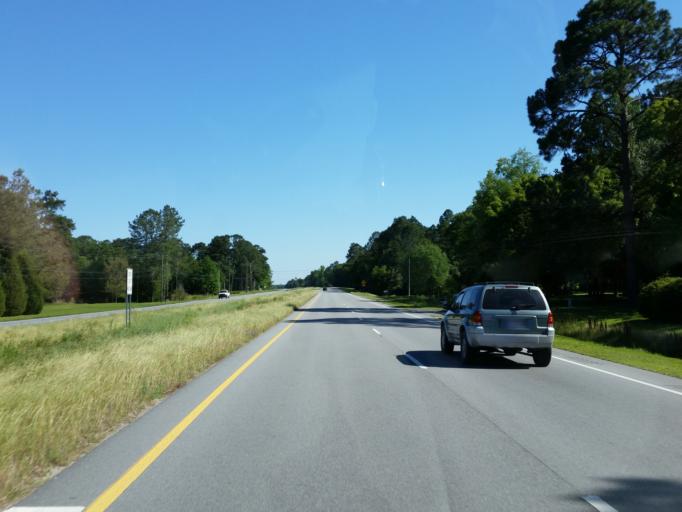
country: US
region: Georgia
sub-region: Lowndes County
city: Valdosta
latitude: 30.7201
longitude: -83.2161
